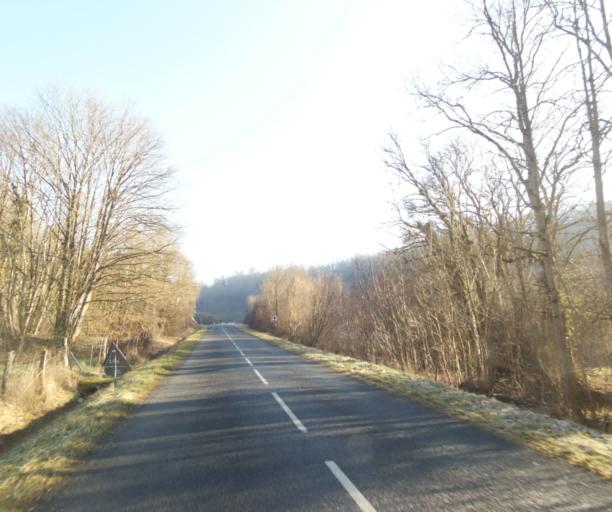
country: FR
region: Champagne-Ardenne
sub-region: Departement de la Haute-Marne
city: Chevillon
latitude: 48.5262
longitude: 5.1581
